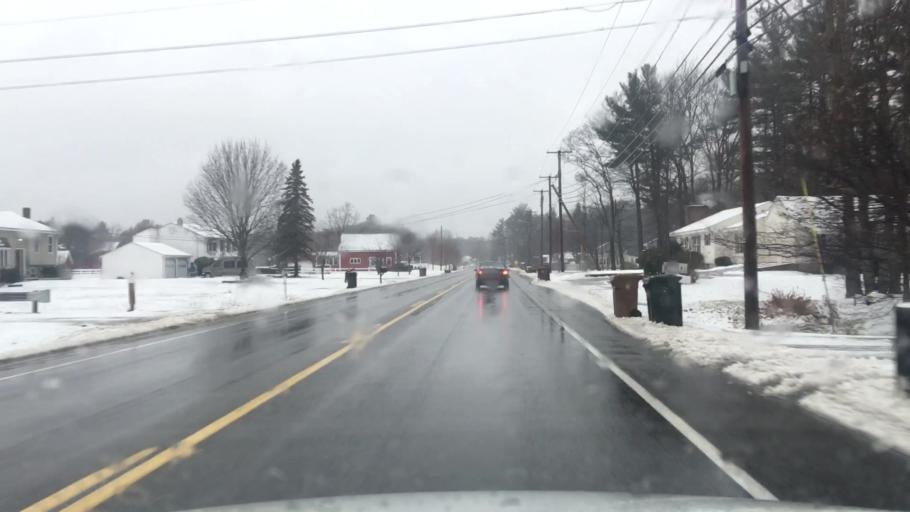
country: US
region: Maine
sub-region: York County
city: Saco
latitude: 43.5418
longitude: -70.4825
